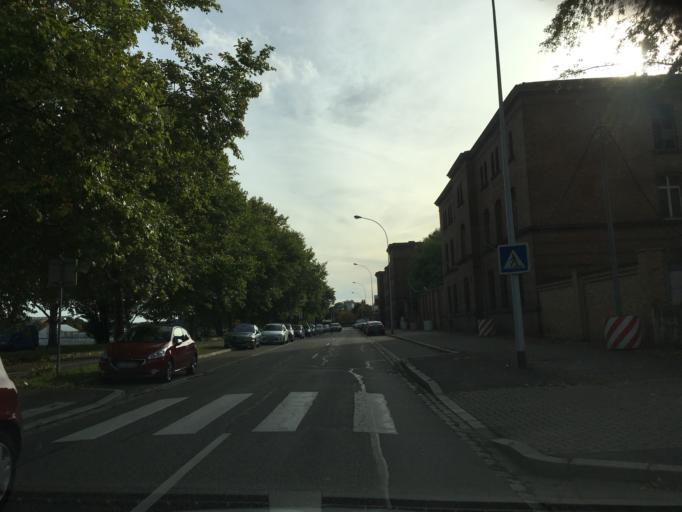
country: DE
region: Baden-Wuerttemberg
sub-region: Freiburg Region
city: Kehl
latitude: 48.5836
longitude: 7.7832
